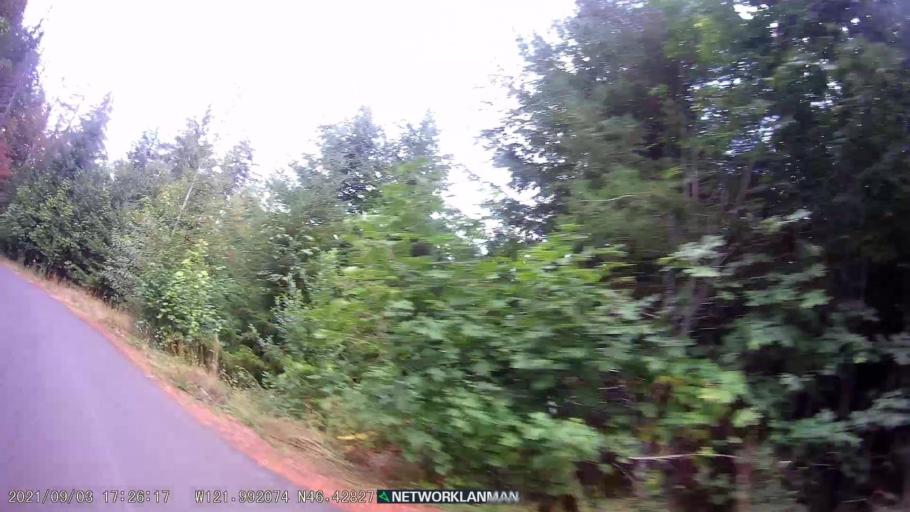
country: US
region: Washington
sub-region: Lewis County
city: Morton
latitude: 46.4282
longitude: -121.9921
